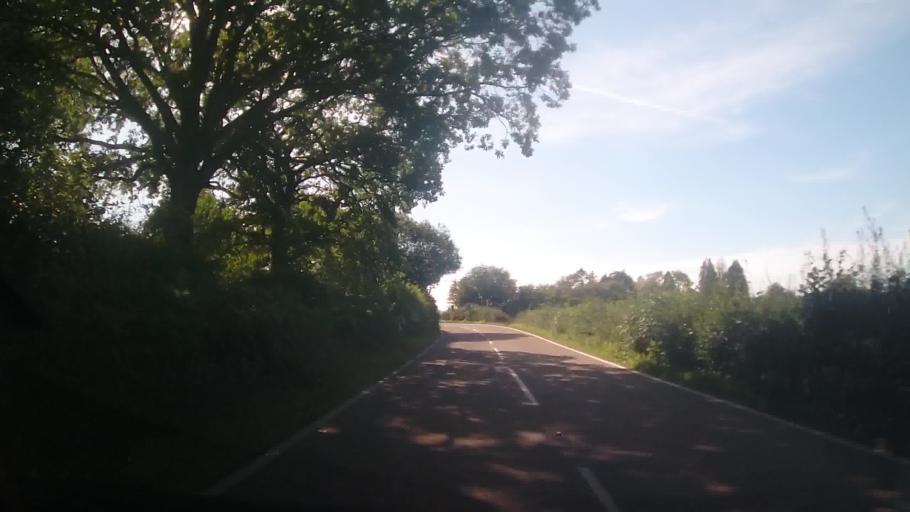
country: GB
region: Wales
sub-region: Sir Powys
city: Mochdre
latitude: 52.4858
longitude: -3.3417
